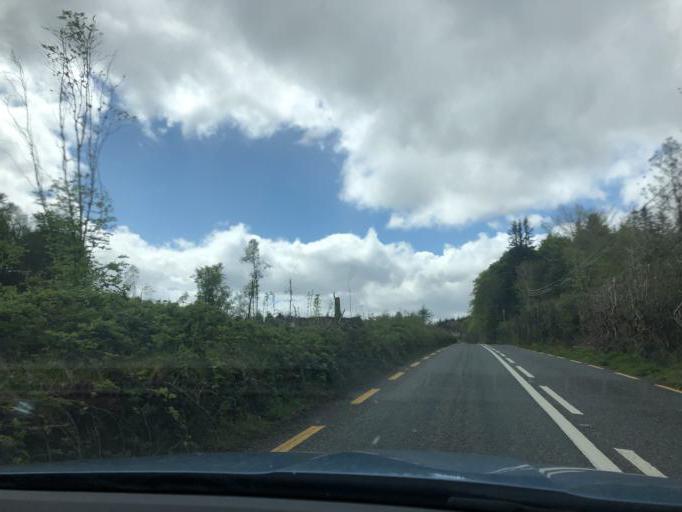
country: IE
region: Munster
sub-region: Ciarrai
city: Kenmare
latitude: 51.8634
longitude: -9.7037
